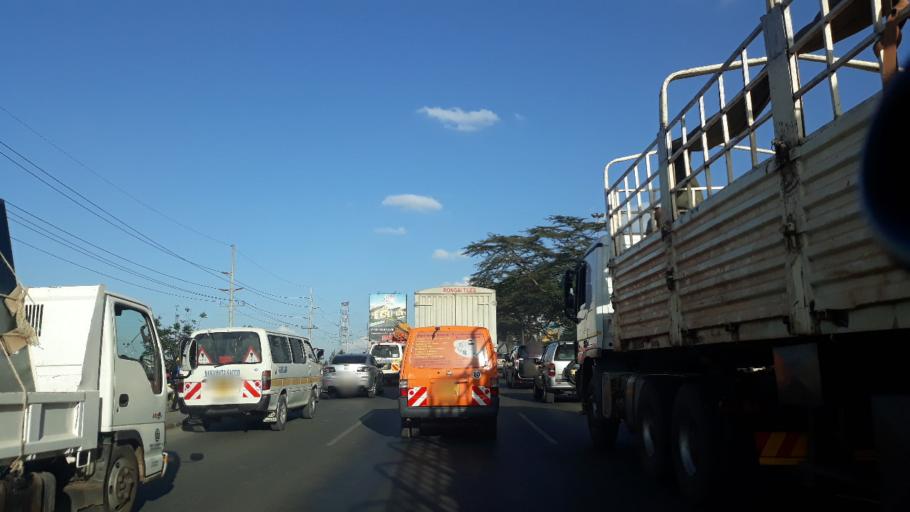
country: KE
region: Nairobi Area
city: Pumwani
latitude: -1.3296
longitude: 36.8720
